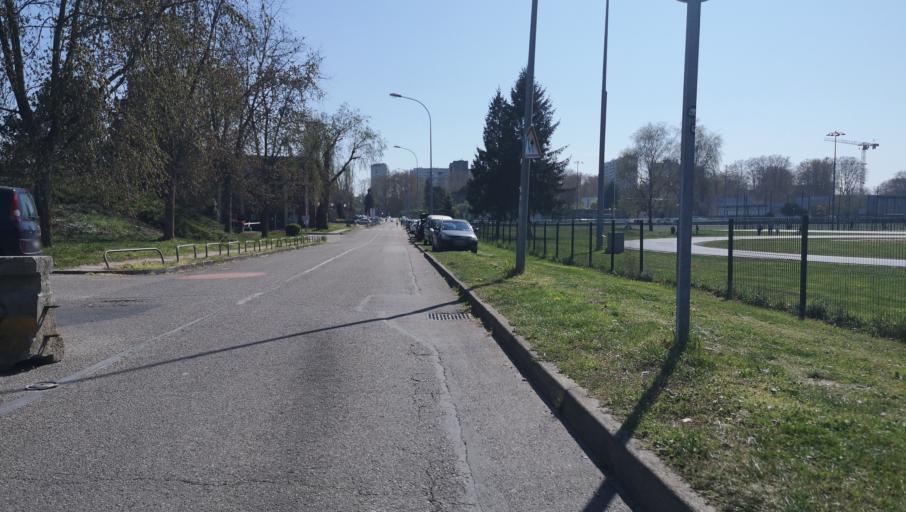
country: FR
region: Rhone-Alpes
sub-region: Departement du Rhone
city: Caluire-et-Cuire
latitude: 45.7839
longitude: 4.8650
